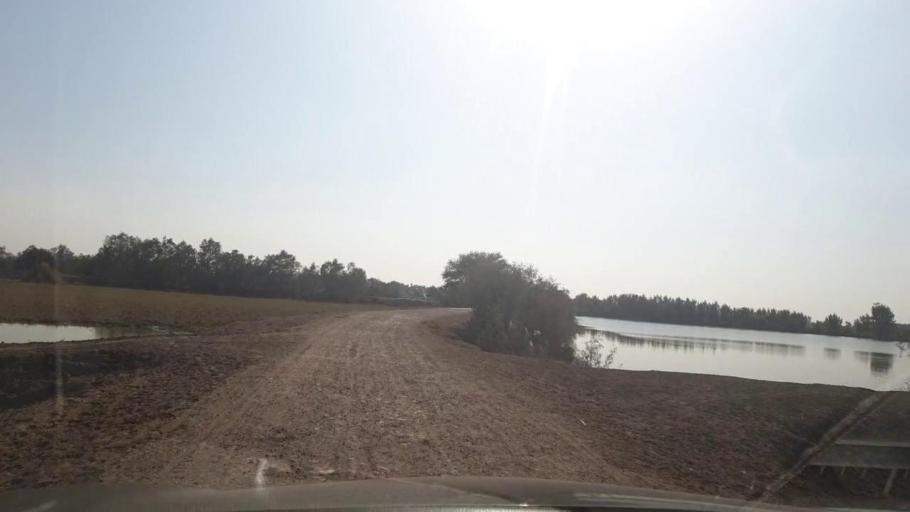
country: PK
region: Sindh
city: Khairpur
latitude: 28.1410
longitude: 69.6023
